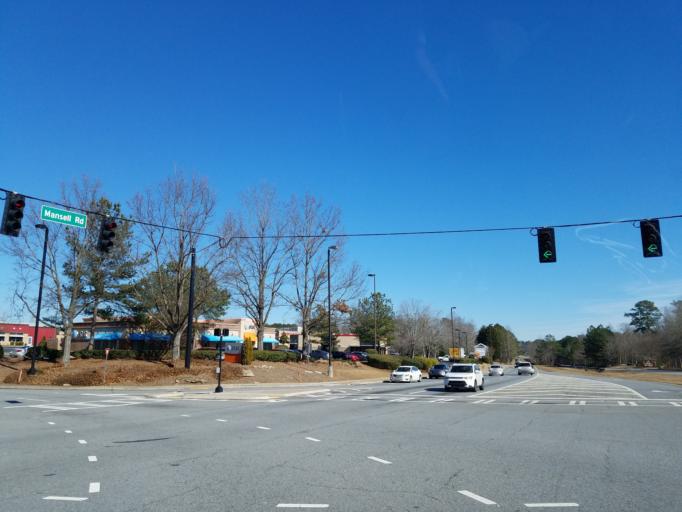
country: US
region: Georgia
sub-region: Fulton County
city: Alpharetta
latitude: 34.0378
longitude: -84.3066
